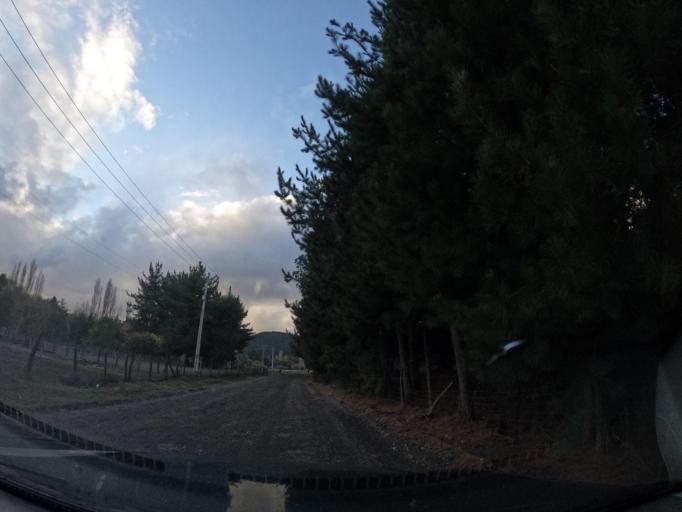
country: CL
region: Biobio
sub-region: Provincia de Concepcion
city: Chiguayante
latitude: -37.0611
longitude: -72.9498
